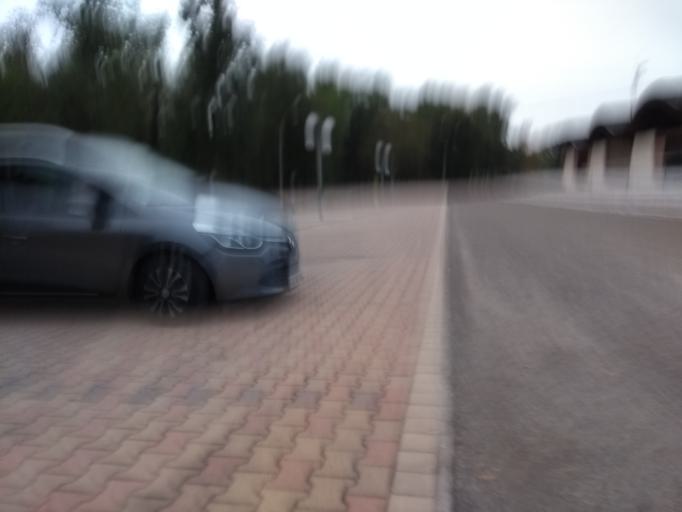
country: FR
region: Aquitaine
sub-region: Departement de la Gironde
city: Talence
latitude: 44.7913
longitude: -0.5978
